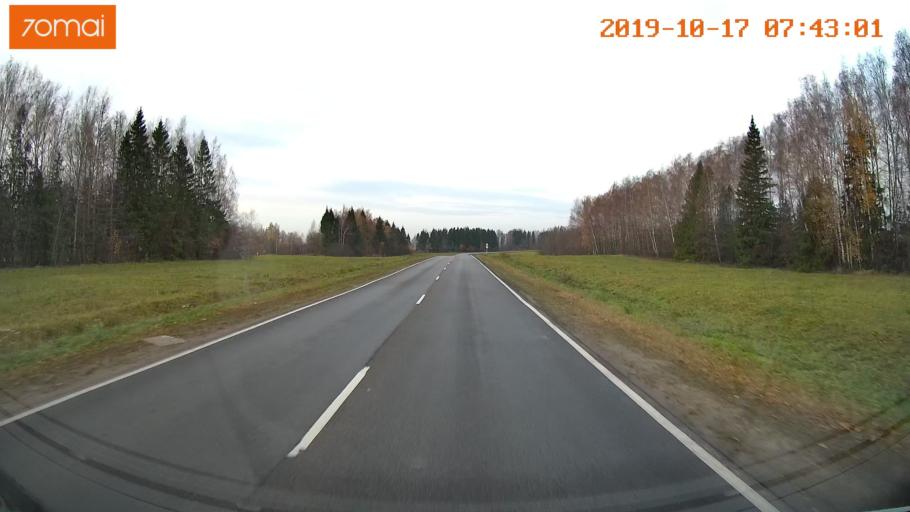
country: RU
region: Vladimir
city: Yur'yev-Pol'skiy
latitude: 56.4832
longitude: 39.7741
